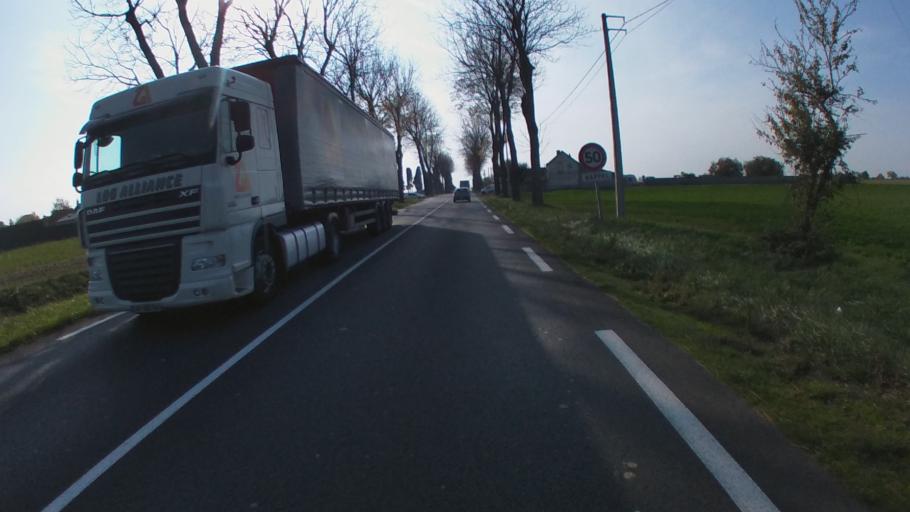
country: FR
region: Pays de la Loire
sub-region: Departement de Maine-et-Loire
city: Distre
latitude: 47.1986
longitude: -0.1240
